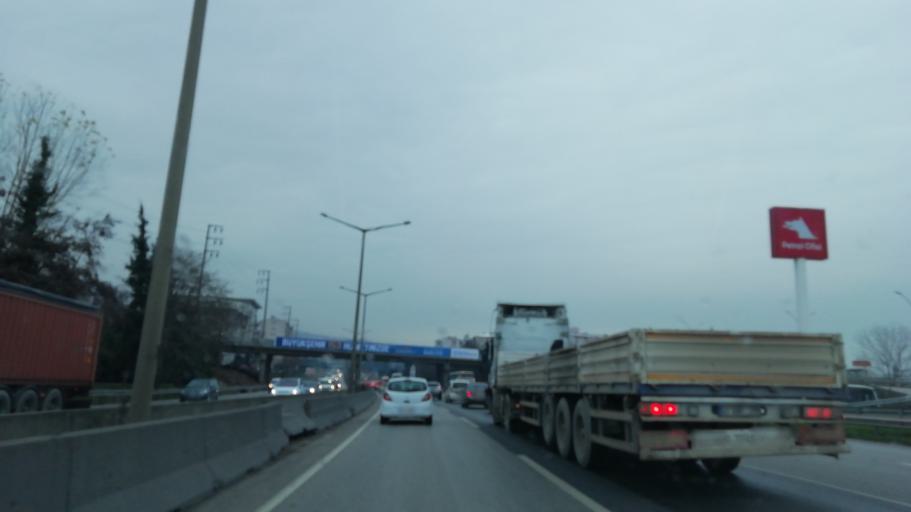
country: TR
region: Kocaeli
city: Izmit
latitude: 40.7631
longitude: 29.8875
